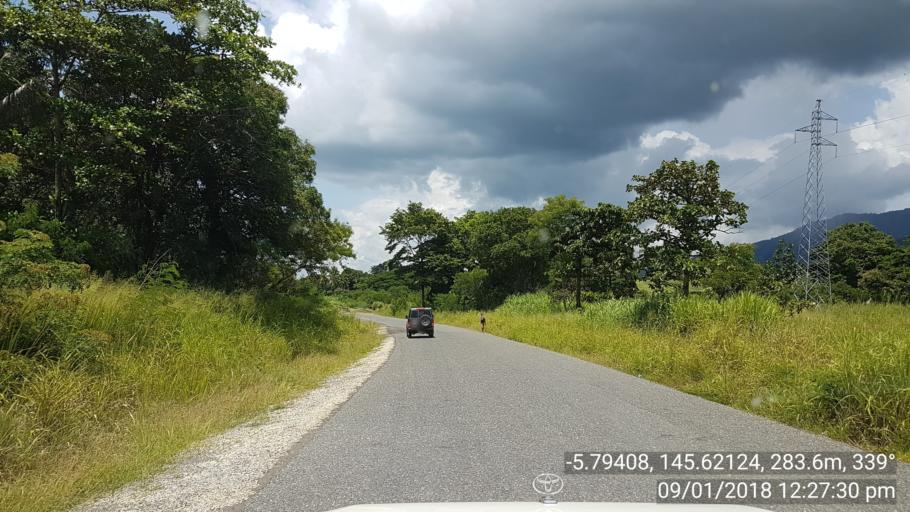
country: PG
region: Eastern Highlands
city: Goroka
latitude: -5.7941
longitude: 145.6213
